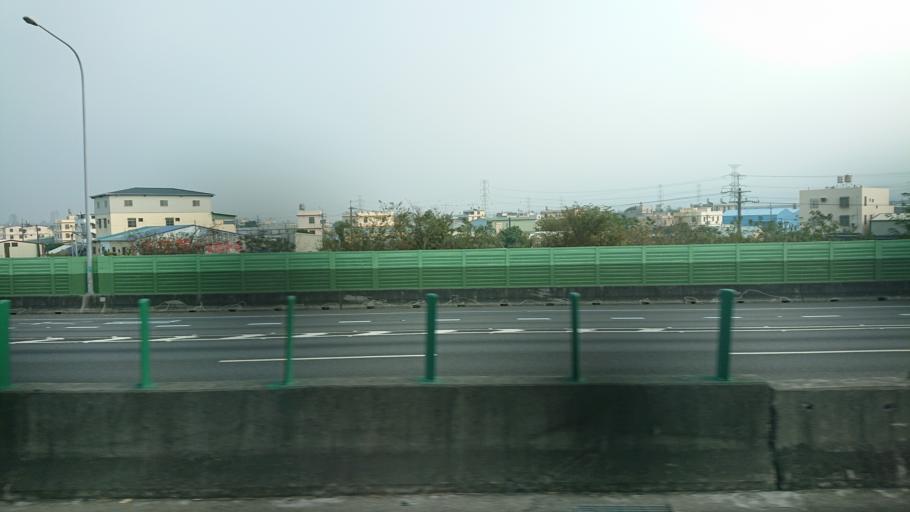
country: TW
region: Taiwan
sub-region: Changhua
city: Chang-hua
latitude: 24.1162
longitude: 120.5712
